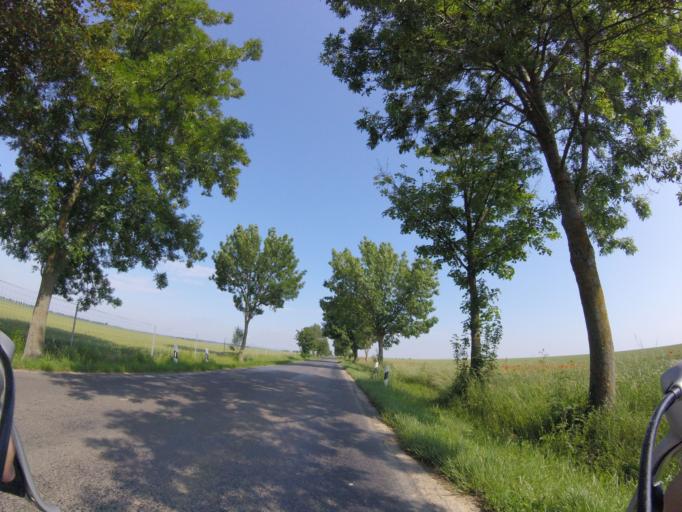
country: HU
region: Baranya
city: Villany
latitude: 45.9203
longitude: 18.3731
